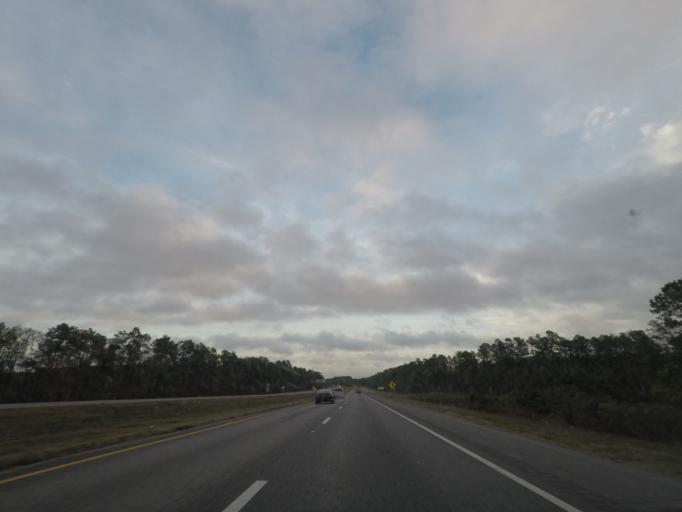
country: US
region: South Carolina
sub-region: Orangeburg County
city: Holly Hill
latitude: 33.3207
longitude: -80.5461
